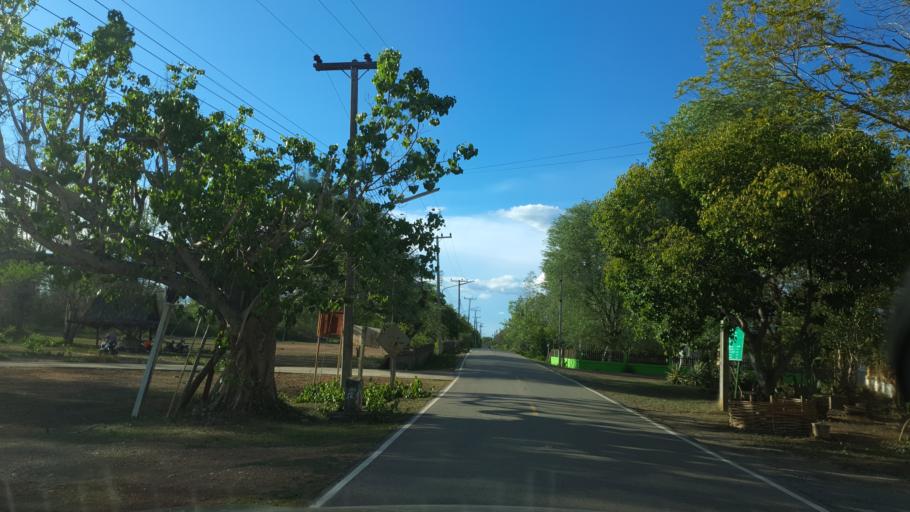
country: TH
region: Lampang
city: Sop Prap
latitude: 17.8817
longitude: 99.3116
